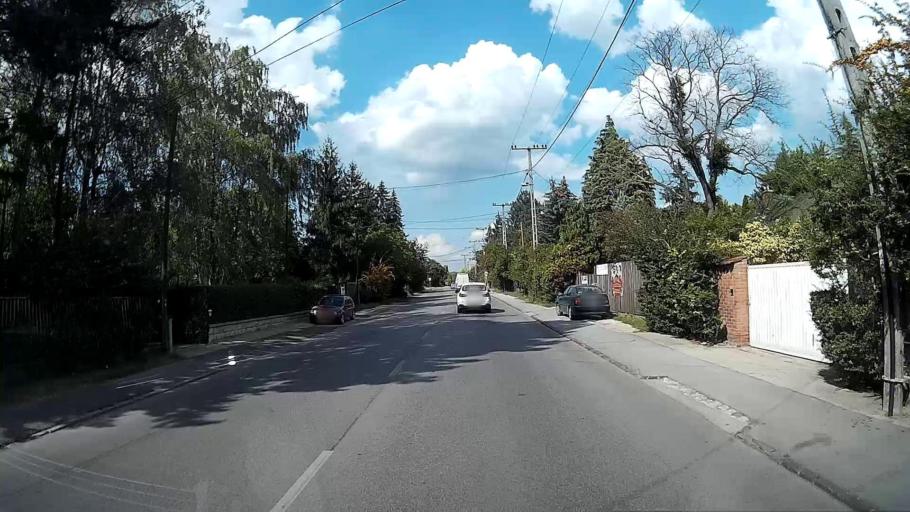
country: HU
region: Pest
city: Leanyfalu
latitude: 47.6964
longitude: 19.0885
